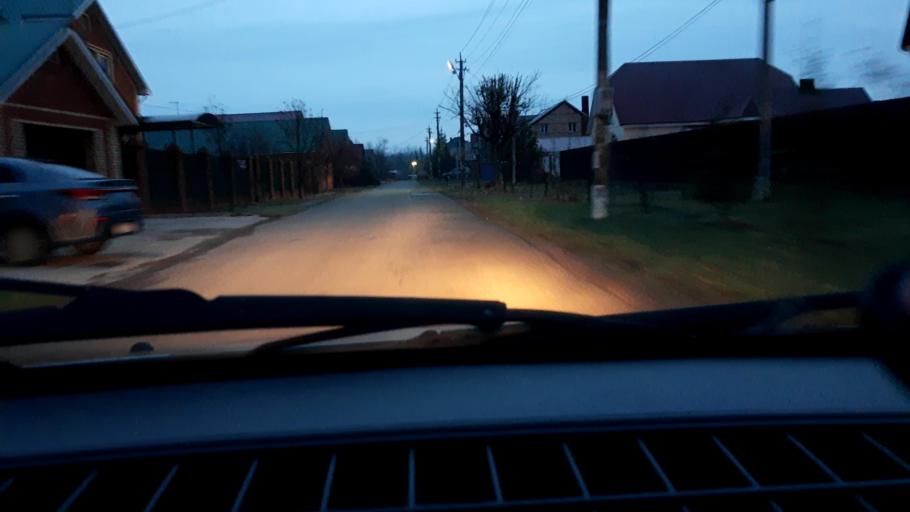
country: RU
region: Bashkortostan
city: Ufa
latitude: 54.6546
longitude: 55.9204
